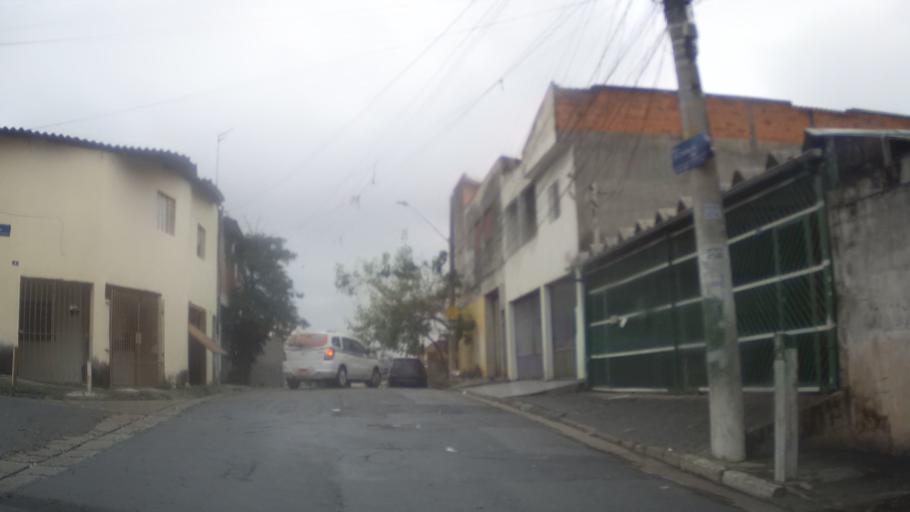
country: BR
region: Sao Paulo
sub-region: Guarulhos
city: Guarulhos
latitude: -23.4398
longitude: -46.5350
